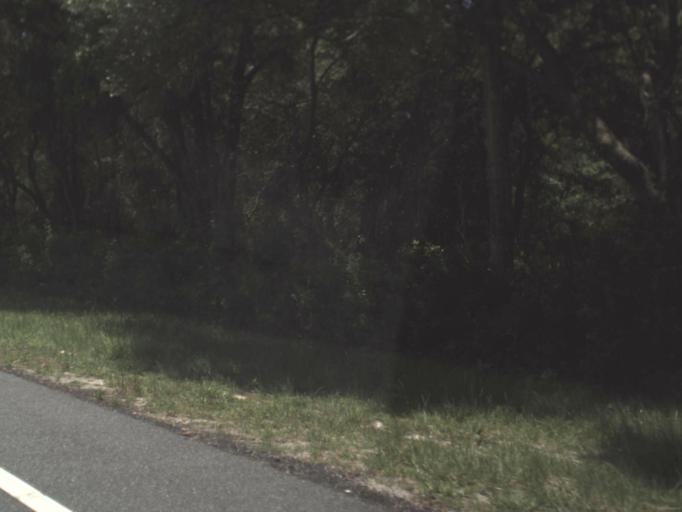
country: US
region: Florida
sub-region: Lafayette County
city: Mayo
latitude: 29.9239
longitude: -82.9505
